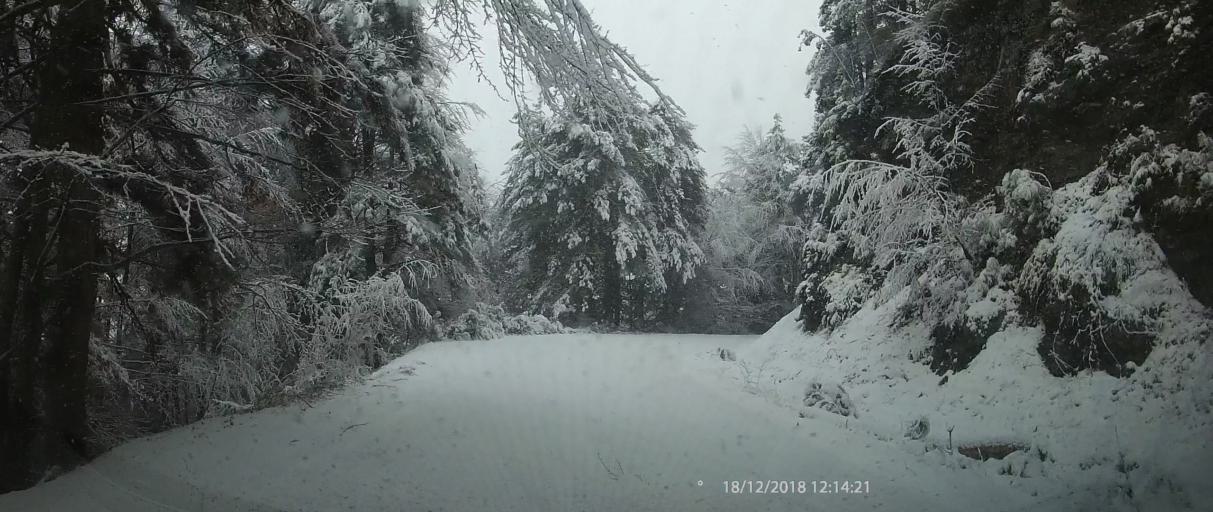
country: GR
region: Central Macedonia
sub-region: Nomos Pierias
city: Litochoro
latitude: 40.1010
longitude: 22.4374
